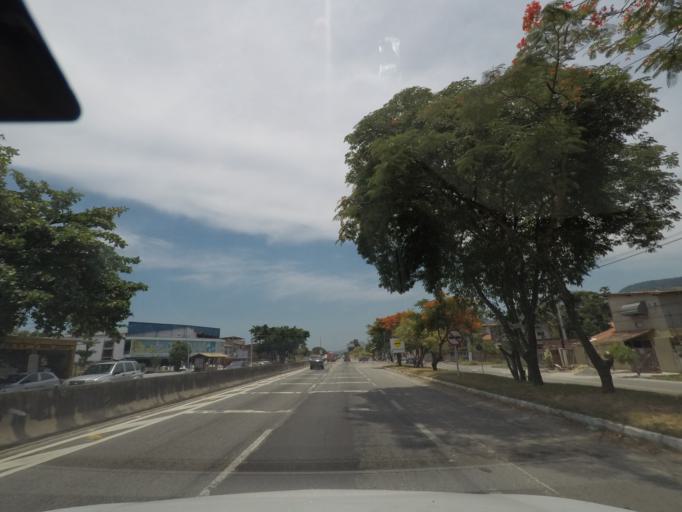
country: BR
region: Rio de Janeiro
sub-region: Marica
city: Marica
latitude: -22.9310
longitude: -42.8775
